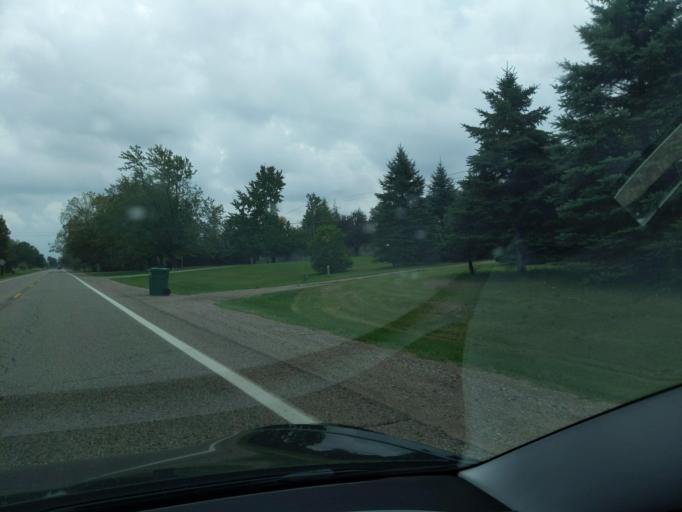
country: US
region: Michigan
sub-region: Eaton County
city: Potterville
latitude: 42.5514
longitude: -84.7566
